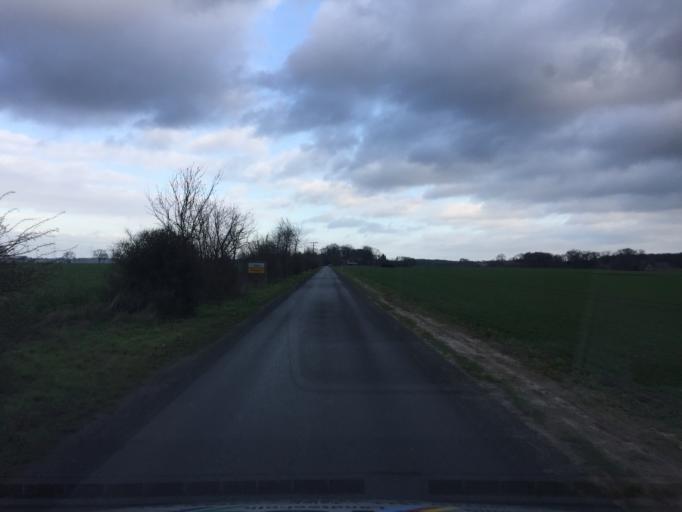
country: DE
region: Lower Saxony
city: Steyerberg
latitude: 52.5115
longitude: 8.9962
